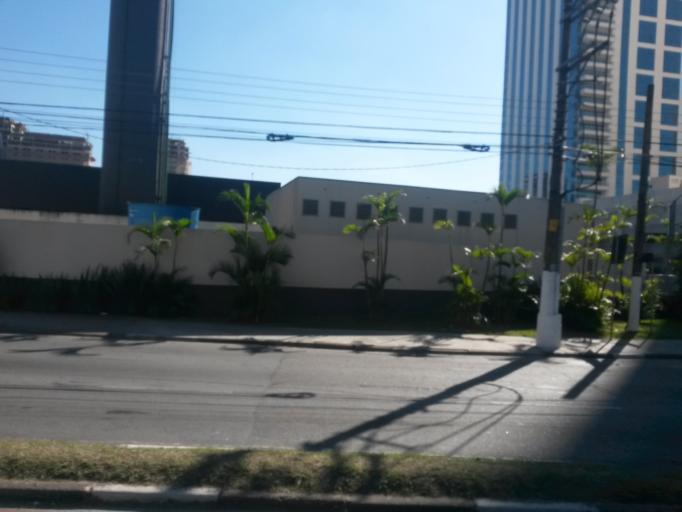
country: BR
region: Sao Paulo
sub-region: Sao Bernardo Do Campo
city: Sao Bernardo do Campo
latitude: -23.6927
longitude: -46.5487
